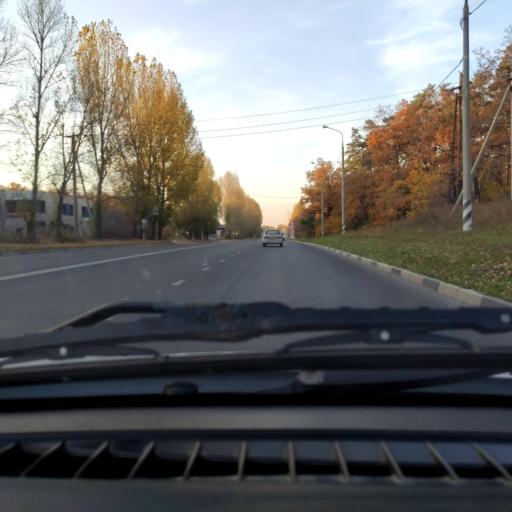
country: RU
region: Samara
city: Zhigulevsk
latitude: 53.5067
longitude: 49.4655
